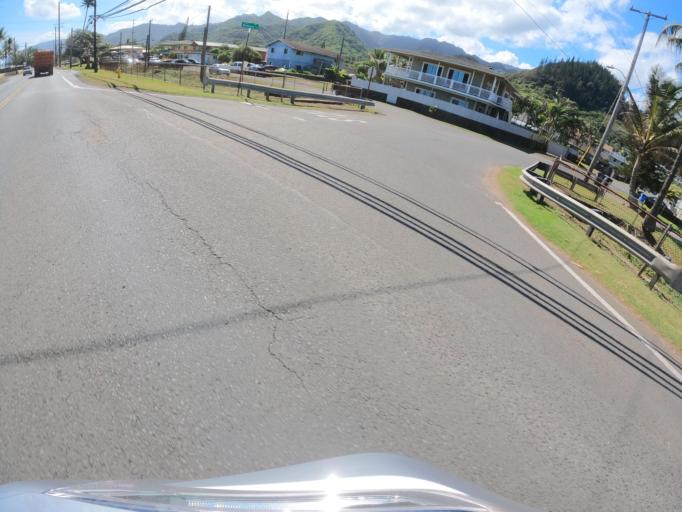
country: US
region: Hawaii
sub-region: Honolulu County
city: Hau'ula
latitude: 21.6140
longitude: -157.9127
